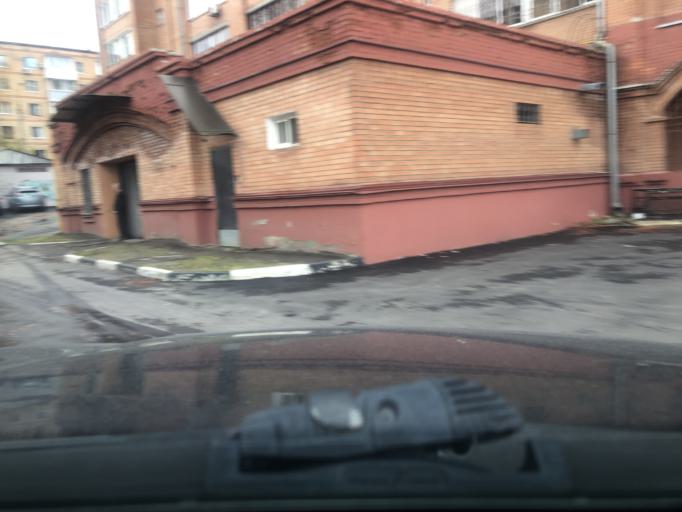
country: RU
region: Moskovskaya
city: Sergiyev Posad
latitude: 56.3201
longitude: 38.1323
